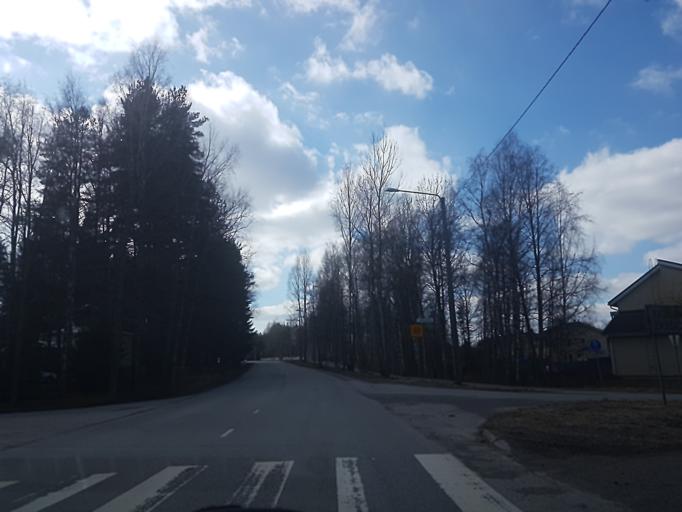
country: FI
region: Uusimaa
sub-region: Porvoo
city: Porvoo
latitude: 60.3925
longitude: 25.6419
